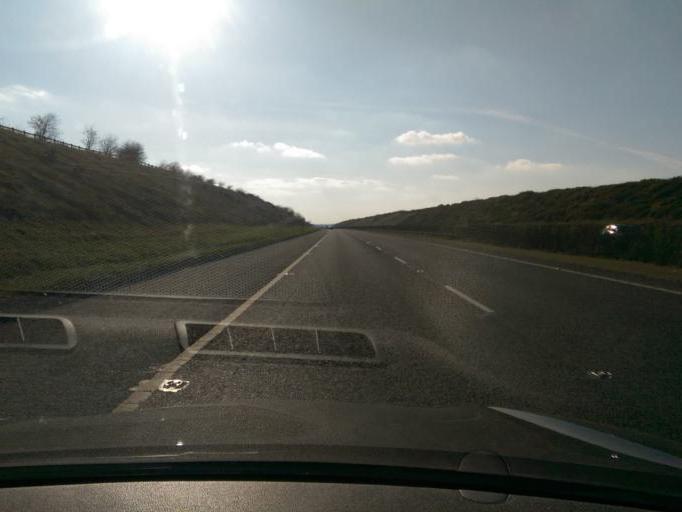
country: IE
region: Leinster
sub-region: Kildare
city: Kildare
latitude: 53.1568
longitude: -6.8636
